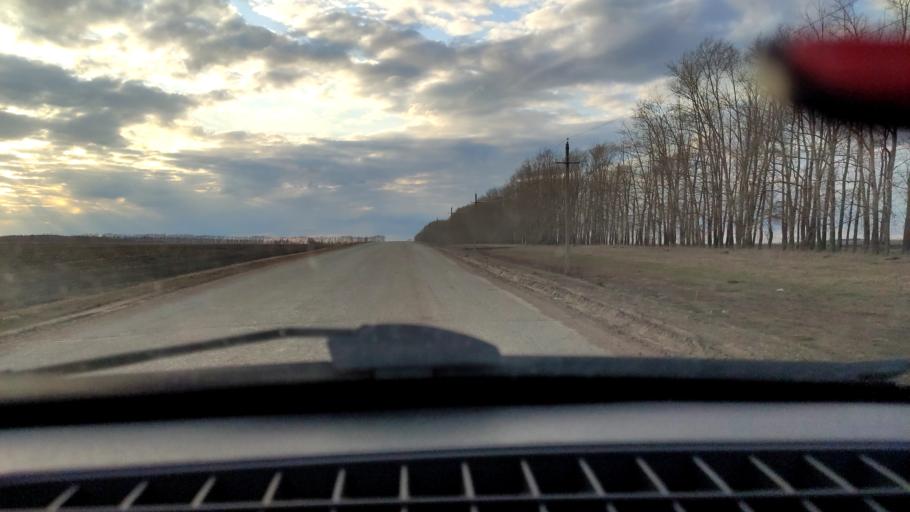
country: RU
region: Bashkortostan
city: Tolbazy
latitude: 53.9858
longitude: 55.7965
